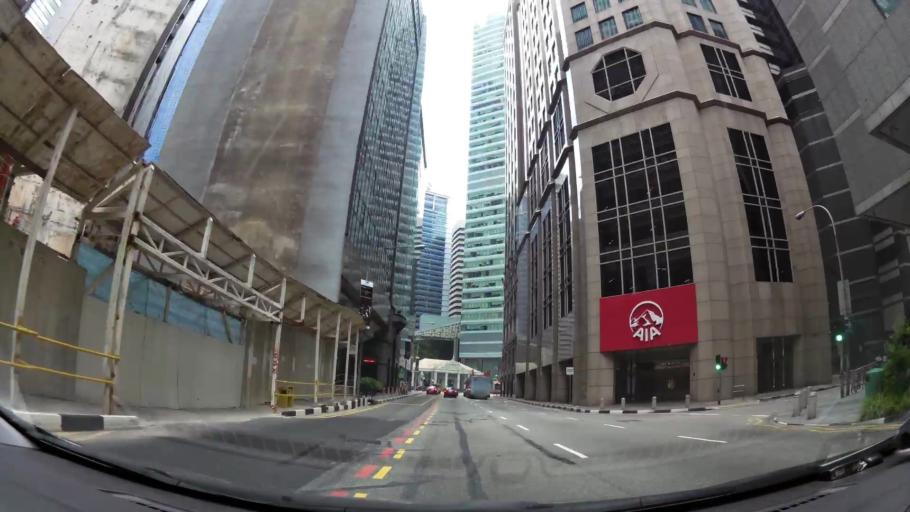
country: SG
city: Singapore
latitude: 1.2817
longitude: 103.8507
